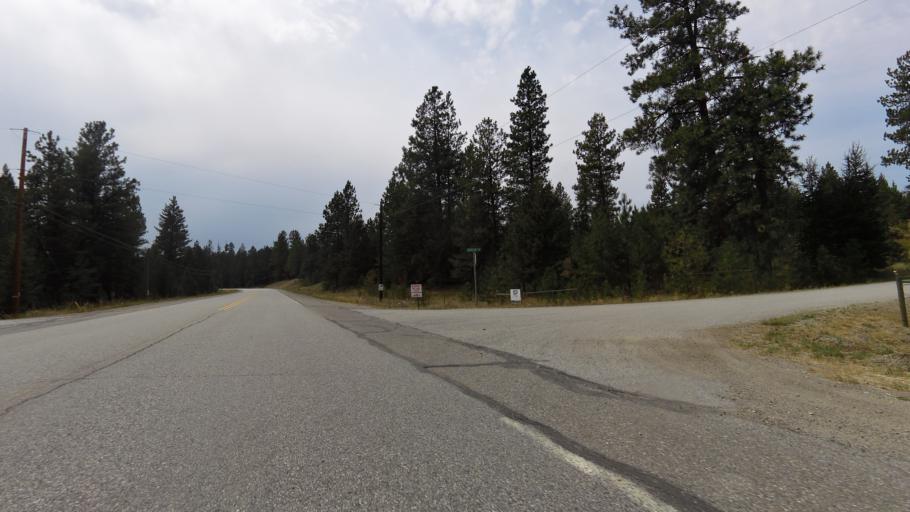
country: US
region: Washington
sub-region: Okanogan County
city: Oroville
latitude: 49.0105
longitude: -119.3066
